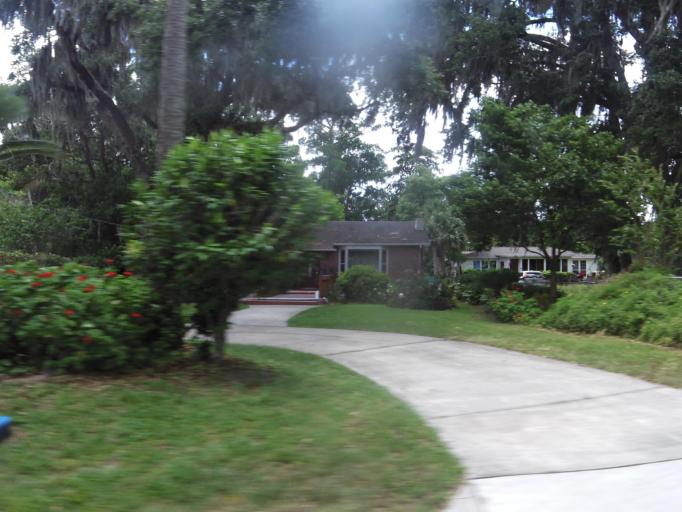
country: US
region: Florida
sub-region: Clay County
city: Orange Park
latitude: 30.1775
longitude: -81.6983
